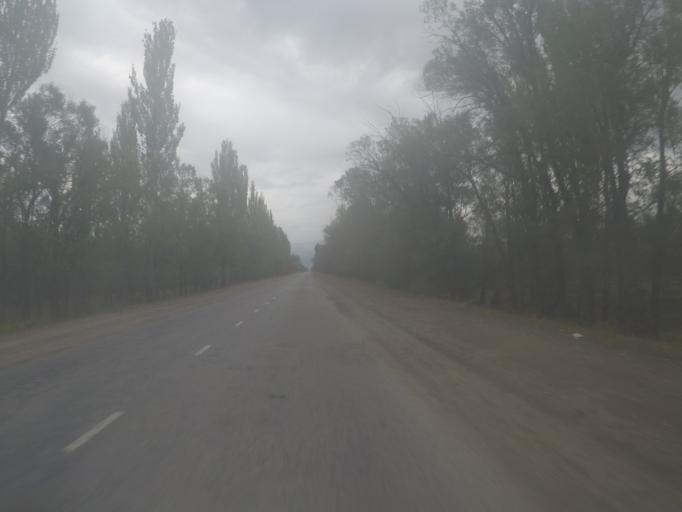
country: KG
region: Ysyk-Koel
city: Tyup
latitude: 42.6294
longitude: 78.3610
